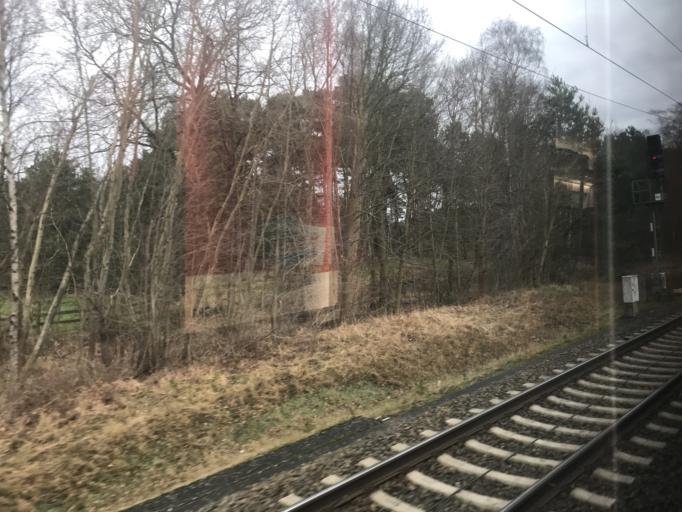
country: DE
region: Lower Saxony
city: Leiferde
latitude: 52.4566
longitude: 10.4303
